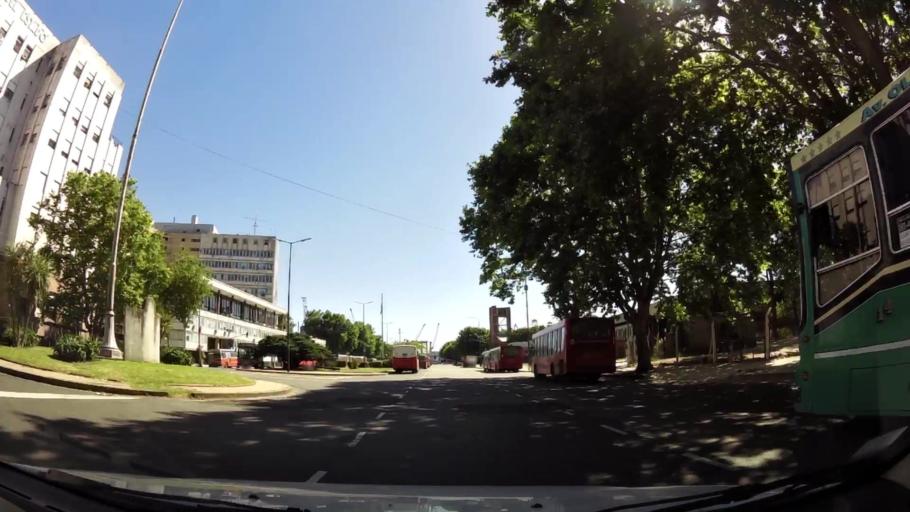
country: AR
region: Buenos Aires F.D.
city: Retiro
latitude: -34.5861
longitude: -58.3703
